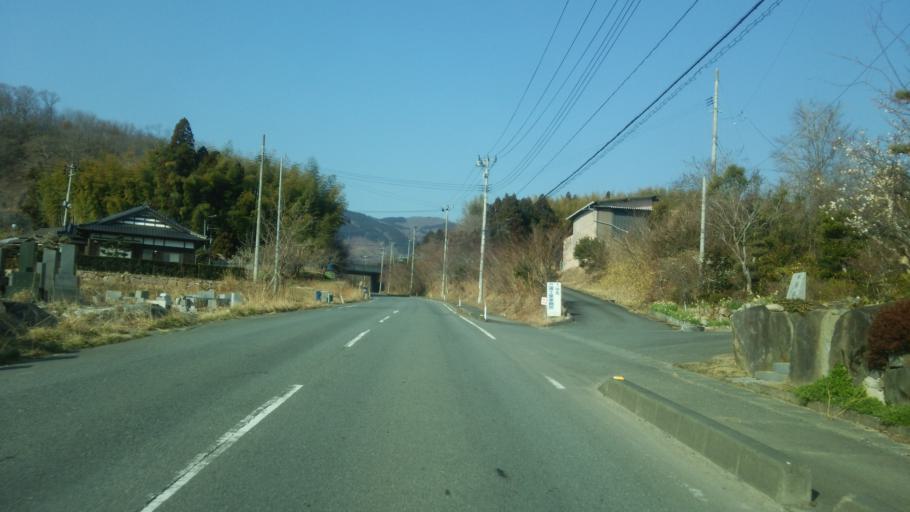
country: JP
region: Fukushima
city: Iwaki
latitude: 37.0405
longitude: 140.8163
